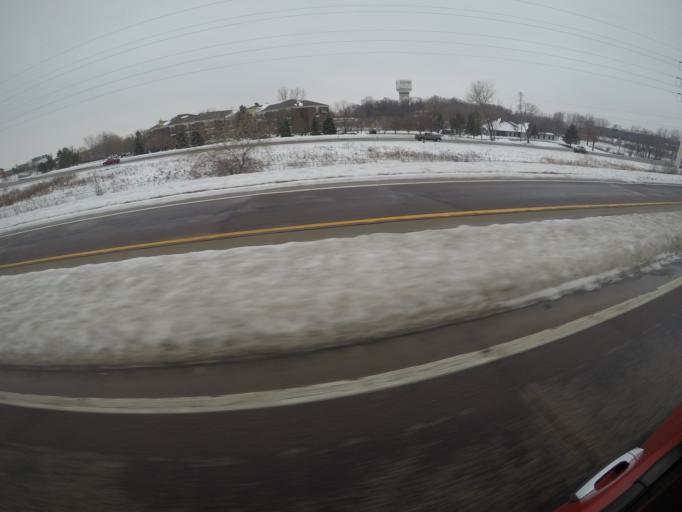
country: US
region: Minnesota
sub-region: Hennepin County
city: Eden Prairie
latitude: 44.8628
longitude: -93.4285
